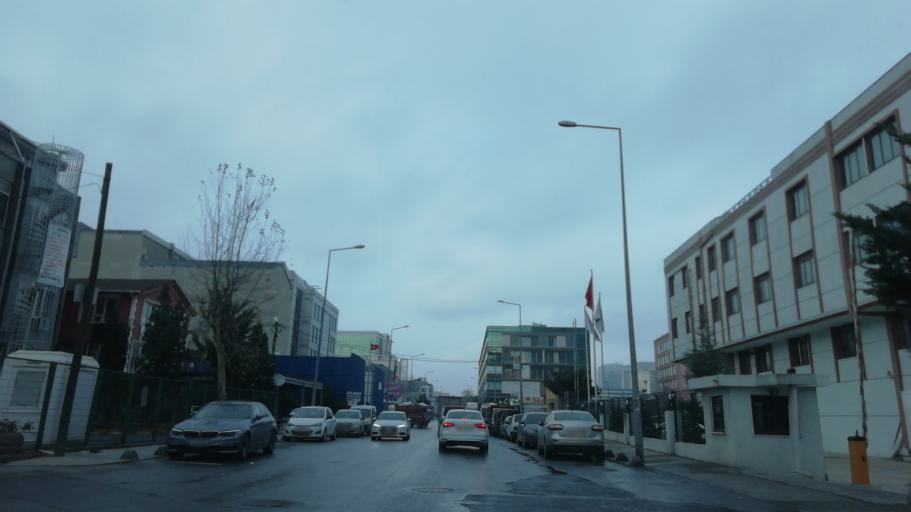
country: TR
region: Istanbul
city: Mahmutbey
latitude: 41.0297
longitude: 28.8070
